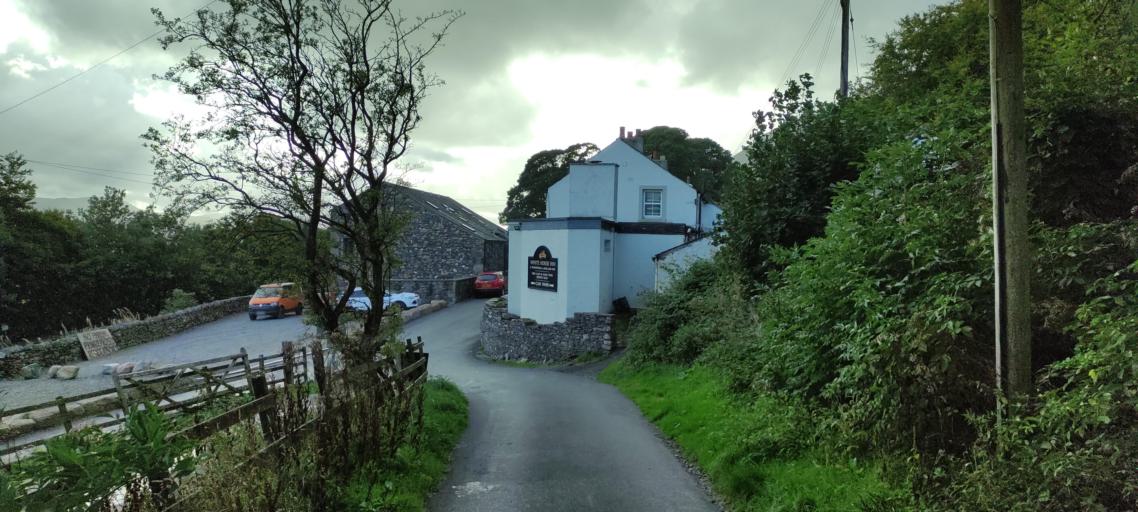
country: GB
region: England
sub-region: Cumbria
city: Keswick
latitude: 54.6333
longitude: -3.0180
